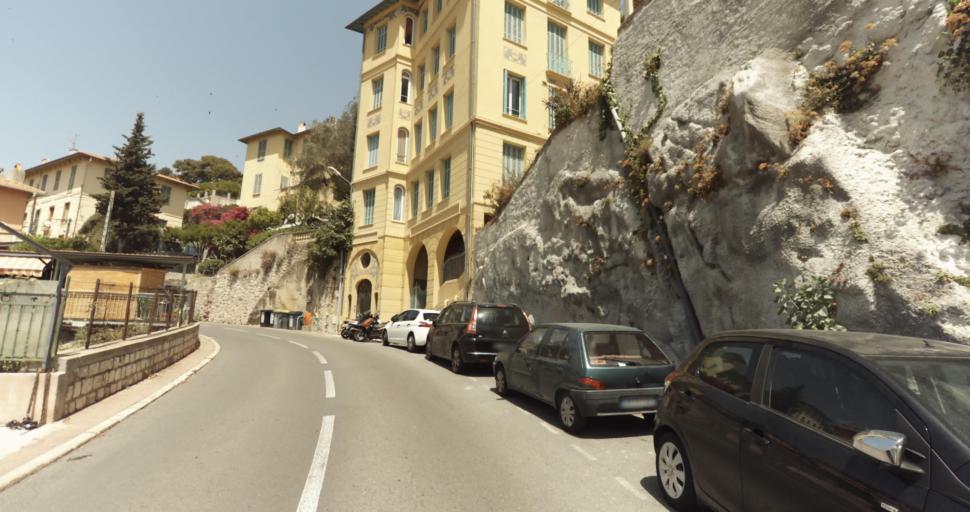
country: FR
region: Provence-Alpes-Cote d'Azur
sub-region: Departement des Alpes-Maritimes
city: Menton
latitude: 43.7786
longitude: 7.5049
